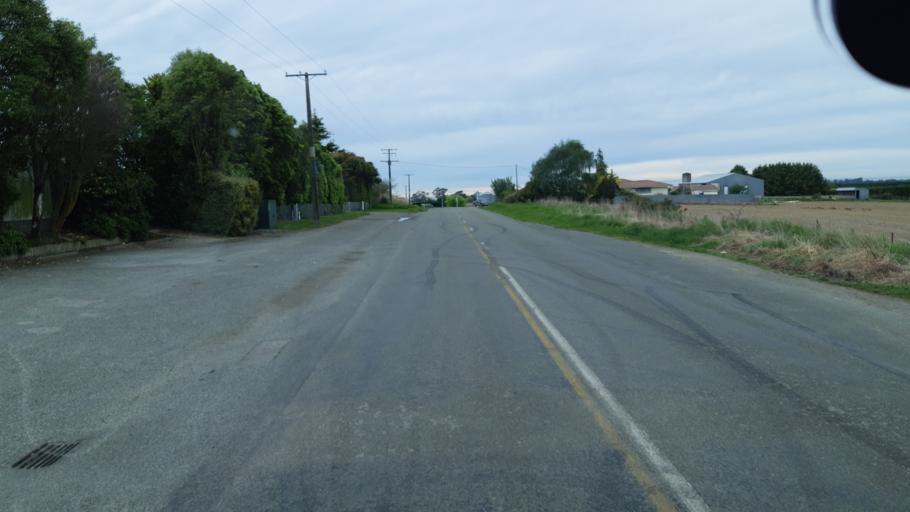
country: NZ
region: Canterbury
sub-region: Timaru District
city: Timaru
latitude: -44.4103
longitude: 171.1716
